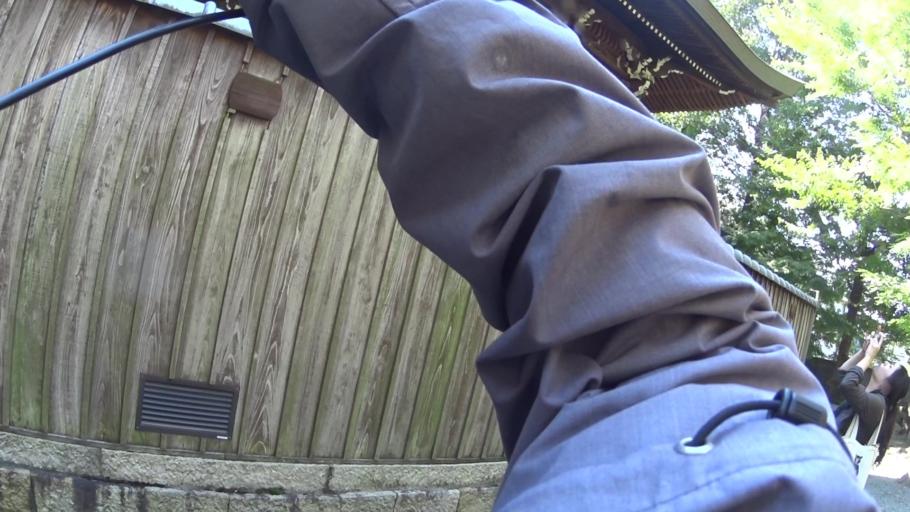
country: JP
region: Osaka
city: Ikeda
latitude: 34.8230
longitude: 135.4220
